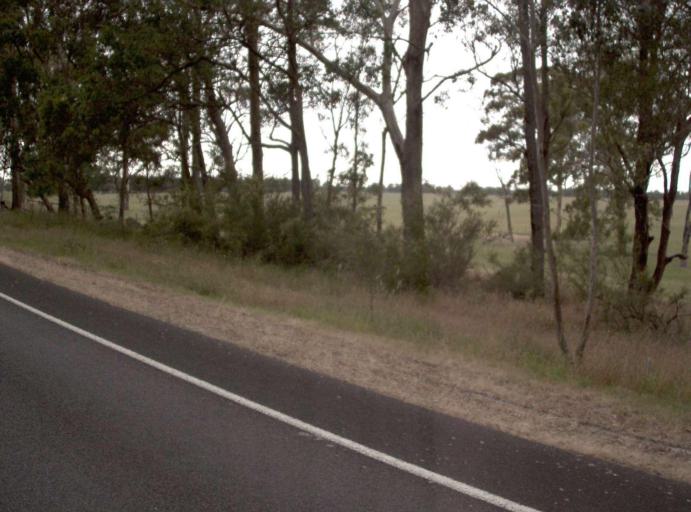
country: AU
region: Victoria
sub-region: Wellington
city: Sale
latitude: -38.4552
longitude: 146.9380
